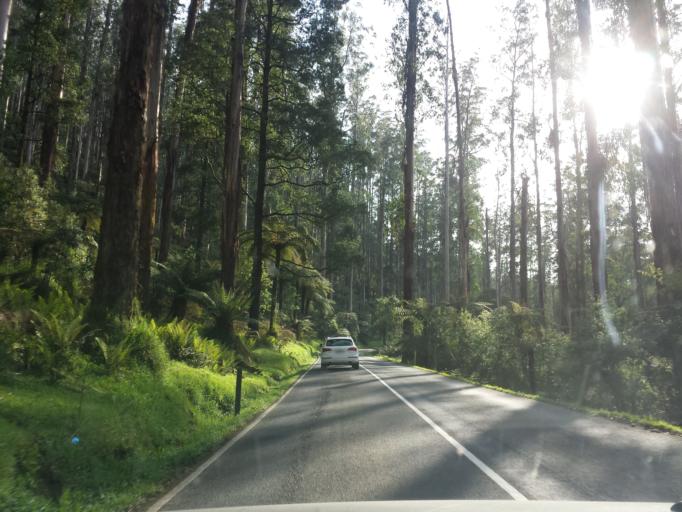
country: AU
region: Victoria
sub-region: Yarra Ranges
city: Healesville
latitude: -37.6065
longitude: 145.6134
